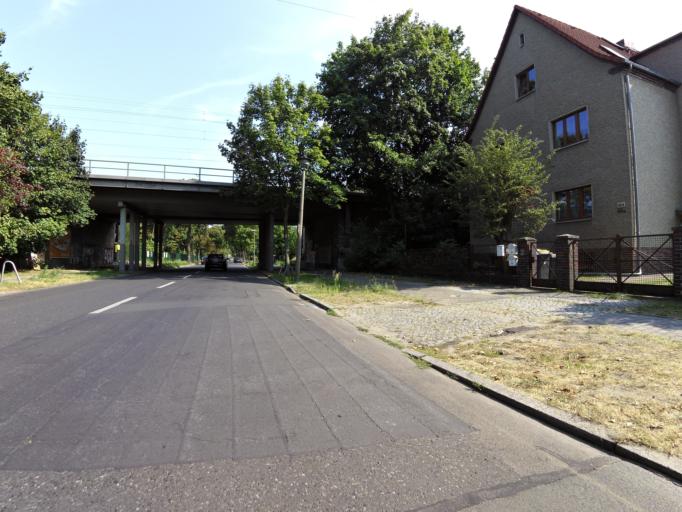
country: DE
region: Berlin
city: Adlershof
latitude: 52.4171
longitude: 13.5550
